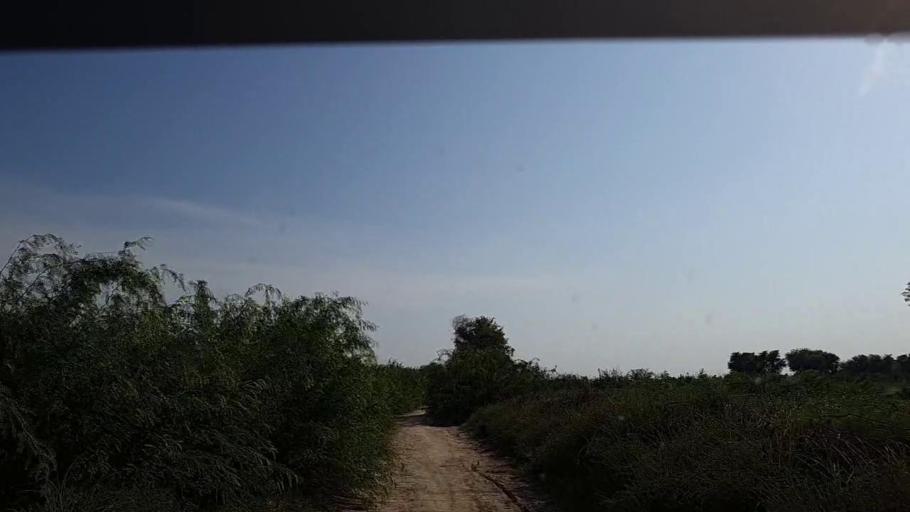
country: PK
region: Sindh
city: Adilpur
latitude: 27.9103
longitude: 69.2381
